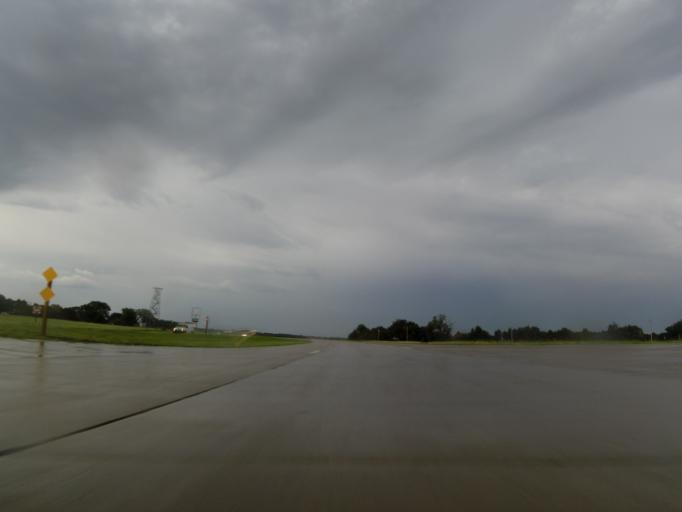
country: US
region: Kansas
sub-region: Reno County
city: Haven
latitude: 37.8990
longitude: -97.7928
